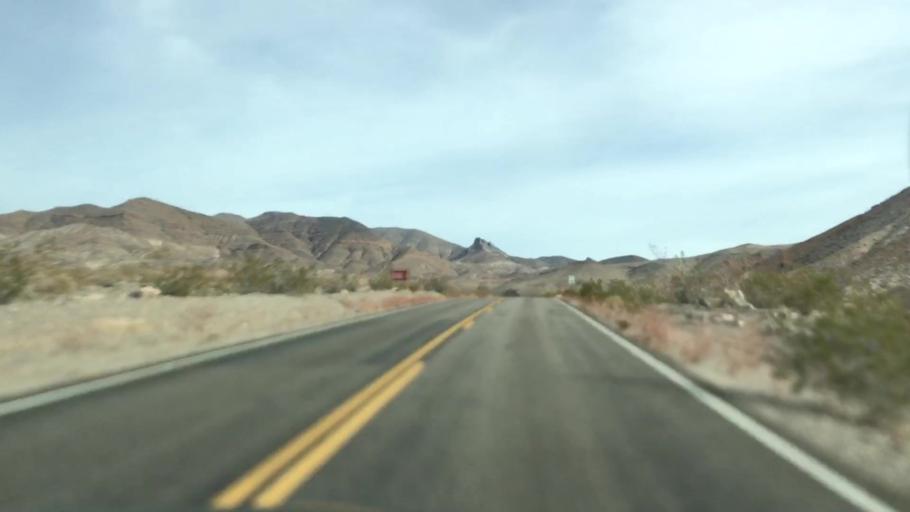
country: US
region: Nevada
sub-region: Nye County
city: Beatty
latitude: 36.7262
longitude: -116.9762
